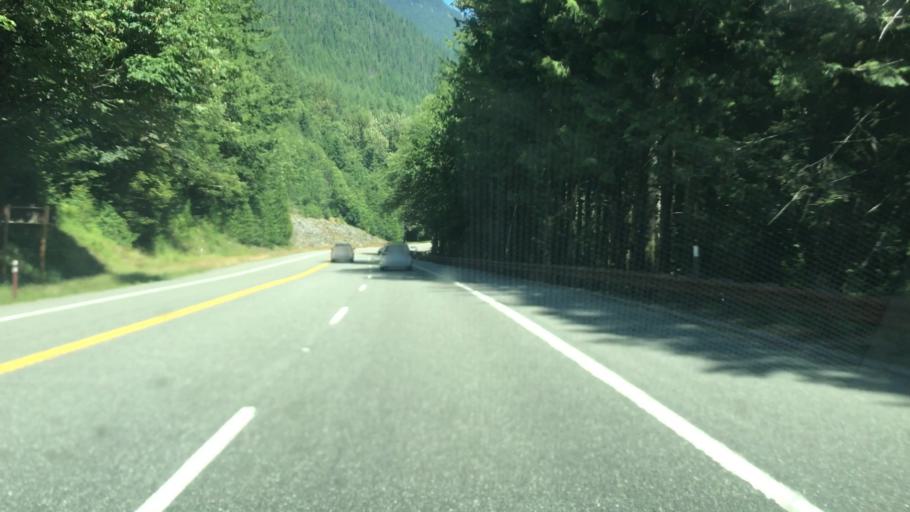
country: US
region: Washington
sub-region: Snohomish County
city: Gold Bar
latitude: 47.7170
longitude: -121.2411
